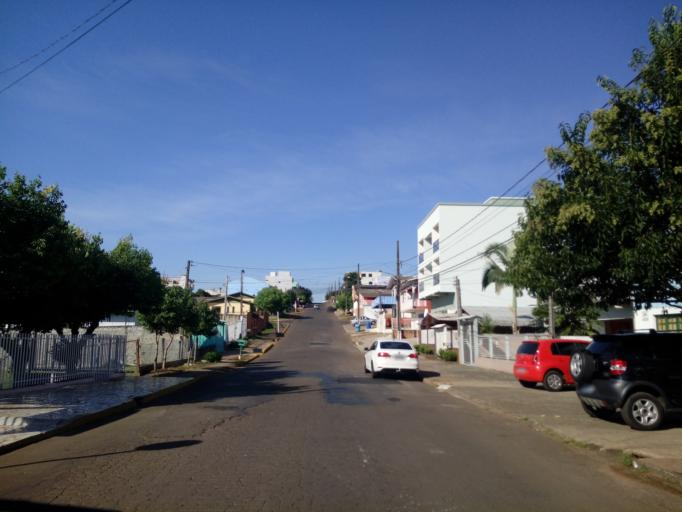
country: BR
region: Santa Catarina
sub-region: Chapeco
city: Chapeco
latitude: -27.0974
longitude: -52.6695
